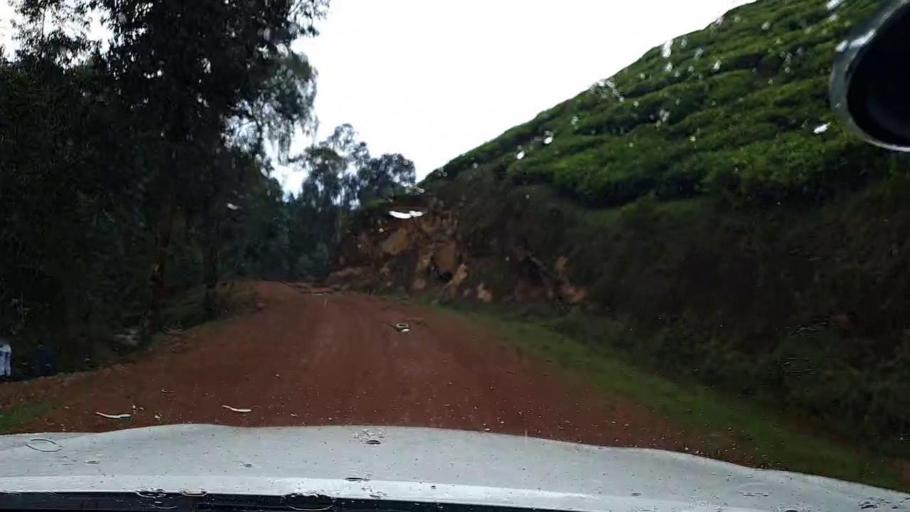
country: RW
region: Western Province
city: Kibuye
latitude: -2.1661
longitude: 29.4356
